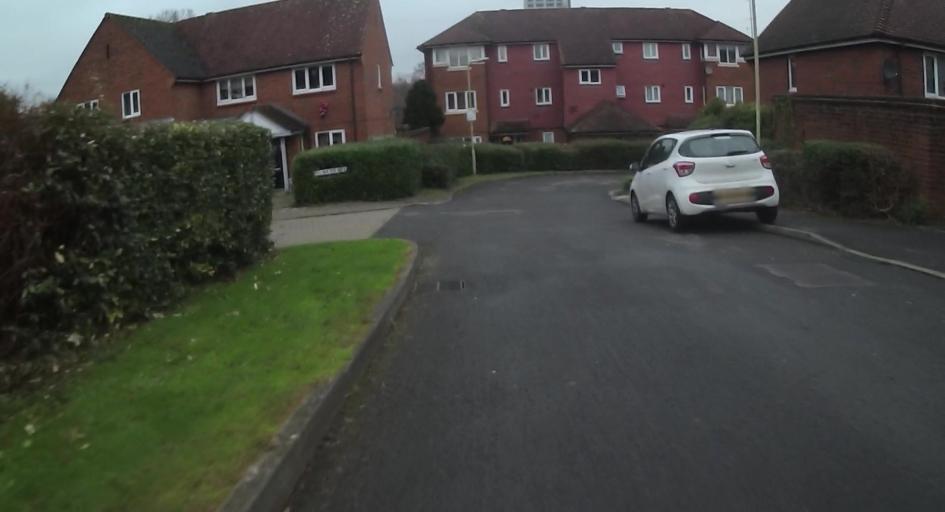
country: GB
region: England
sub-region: Hampshire
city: Basingstoke
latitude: 51.2656
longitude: -1.0699
